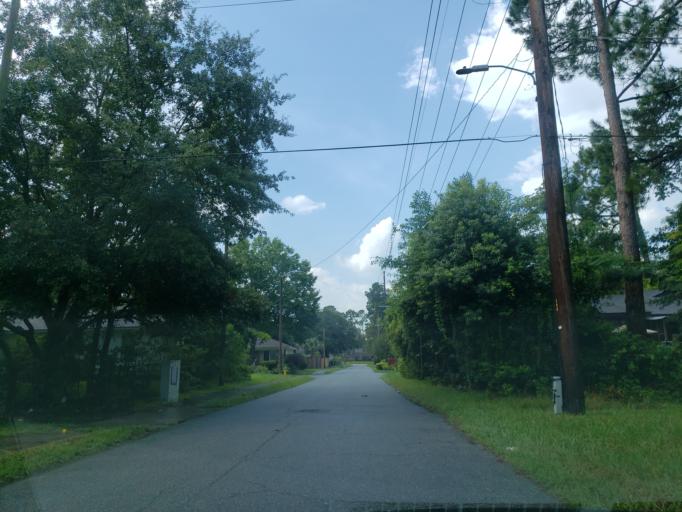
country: US
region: Georgia
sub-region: Chatham County
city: Thunderbolt
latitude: 32.0334
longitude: -81.0794
